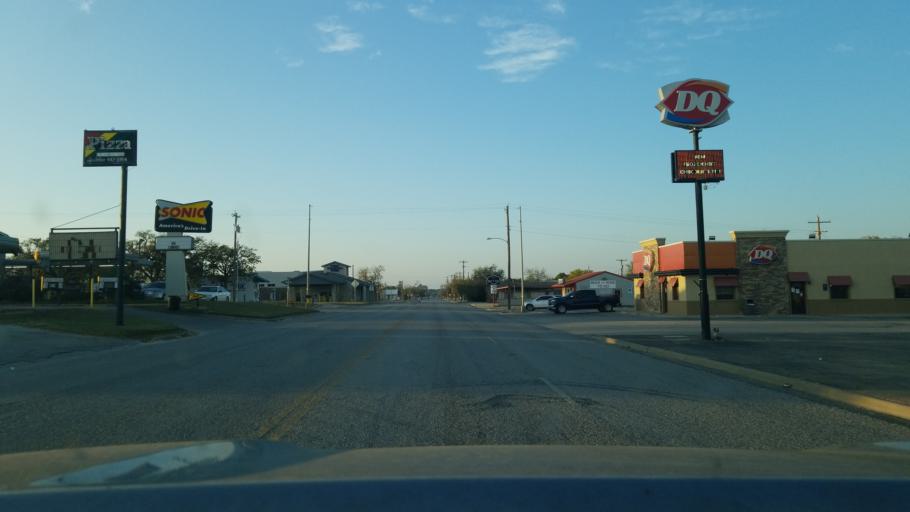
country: US
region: Texas
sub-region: Eastland County
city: Cisco
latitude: 32.3761
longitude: -98.9714
